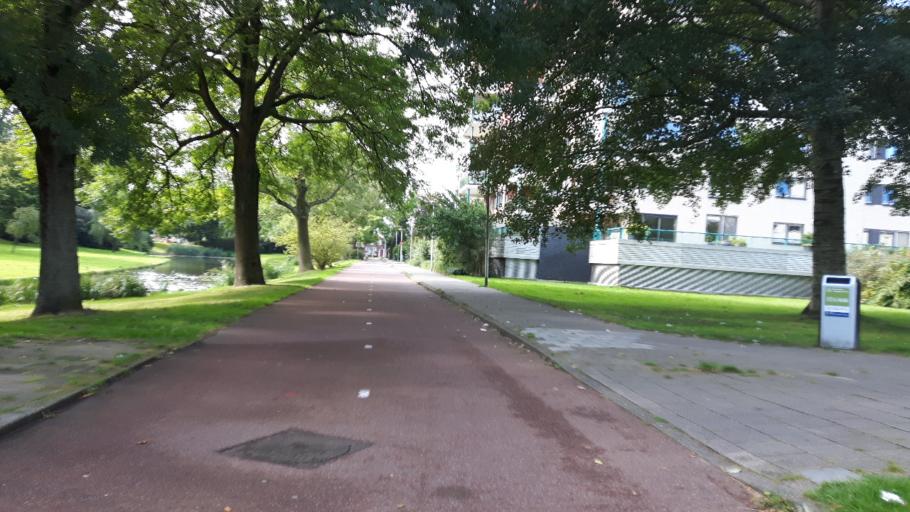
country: NL
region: North Holland
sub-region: Gemeente Purmerend
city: Purmerend
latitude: 52.5059
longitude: 4.9545
